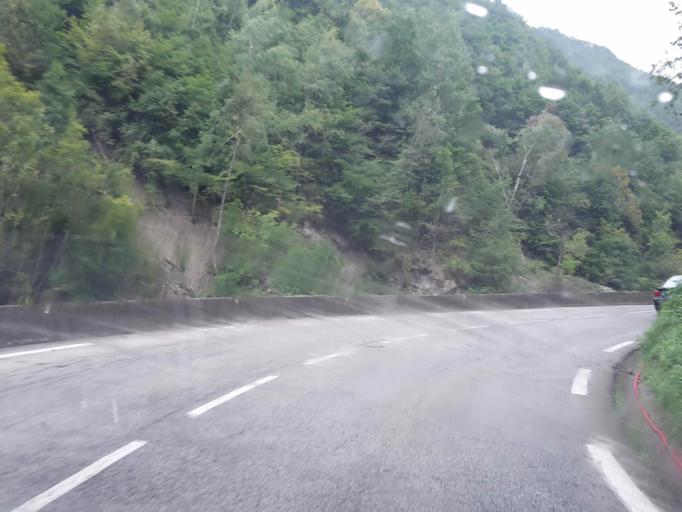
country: FR
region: Rhone-Alpes
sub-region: Departement de la Savoie
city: Ugine
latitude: 45.7522
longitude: 6.4494
